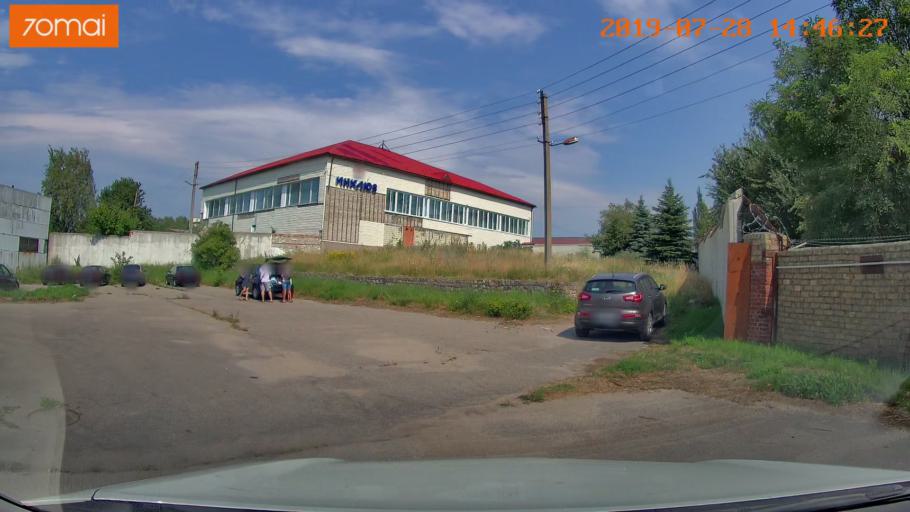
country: RU
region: Kaliningrad
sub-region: Gorod Kaliningrad
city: Yantarnyy
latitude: 54.8755
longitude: 19.9395
